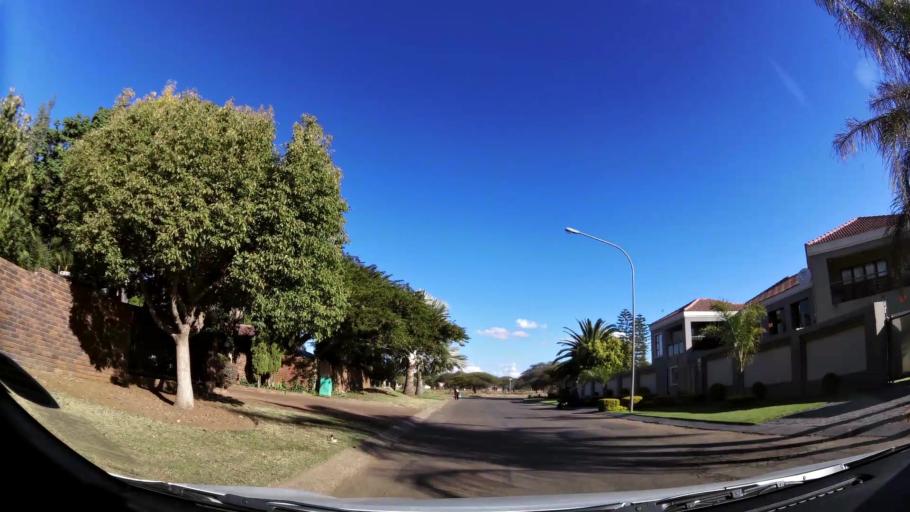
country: ZA
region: Limpopo
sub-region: Capricorn District Municipality
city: Polokwane
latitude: -23.8823
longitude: 29.4922
